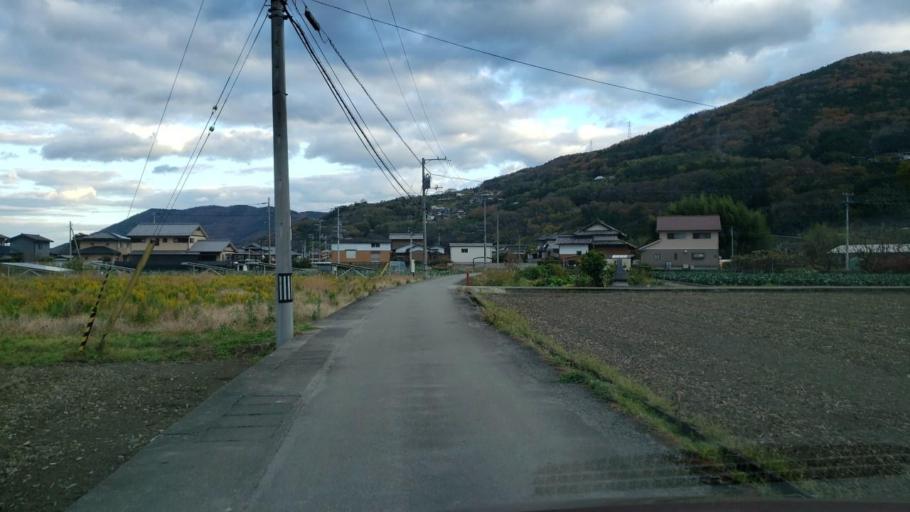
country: JP
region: Tokushima
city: Wakimachi
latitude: 34.0578
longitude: 134.1434
